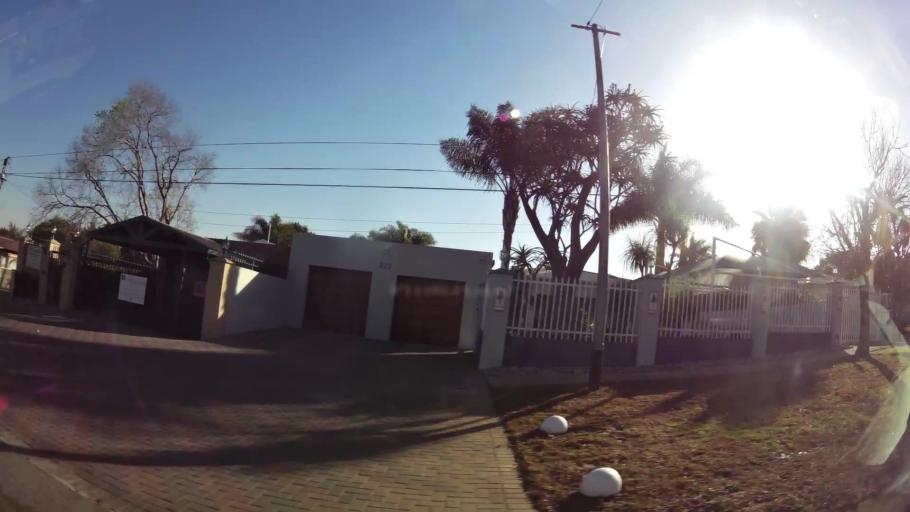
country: ZA
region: Gauteng
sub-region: City of Tshwane Metropolitan Municipality
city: Pretoria
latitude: -25.6987
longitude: 28.2427
